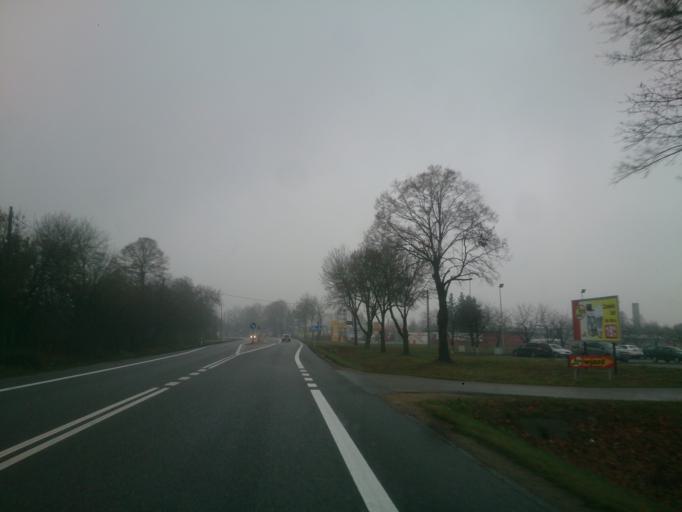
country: PL
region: Masovian Voivodeship
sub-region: Powiat sierpecki
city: Sierpc
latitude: 52.8586
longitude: 19.6807
